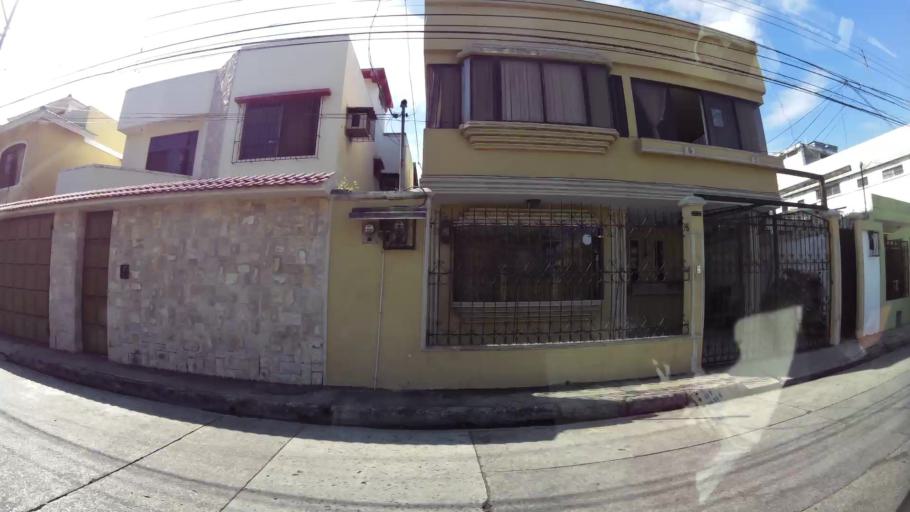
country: EC
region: Guayas
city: Guayaquil
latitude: -2.2295
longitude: -79.8909
